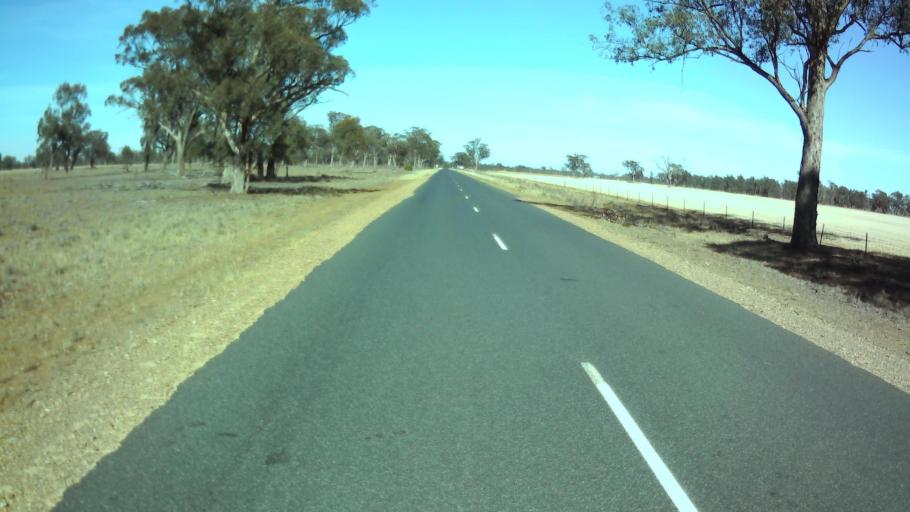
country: AU
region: New South Wales
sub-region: Weddin
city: Grenfell
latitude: -34.1366
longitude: 147.7657
